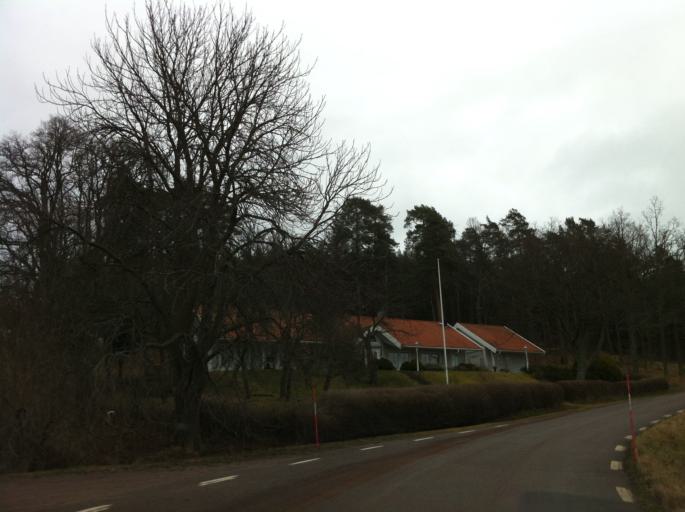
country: SE
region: Kalmar
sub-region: Vasterviks Kommun
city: Vaestervik
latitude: 57.9091
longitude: 16.6554
